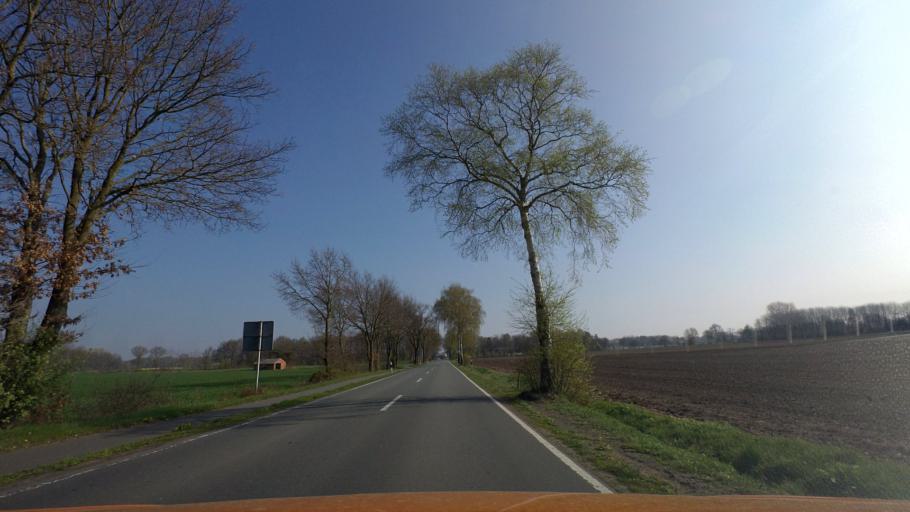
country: DE
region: Lower Saxony
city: Bakum
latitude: 52.7153
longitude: 8.1628
